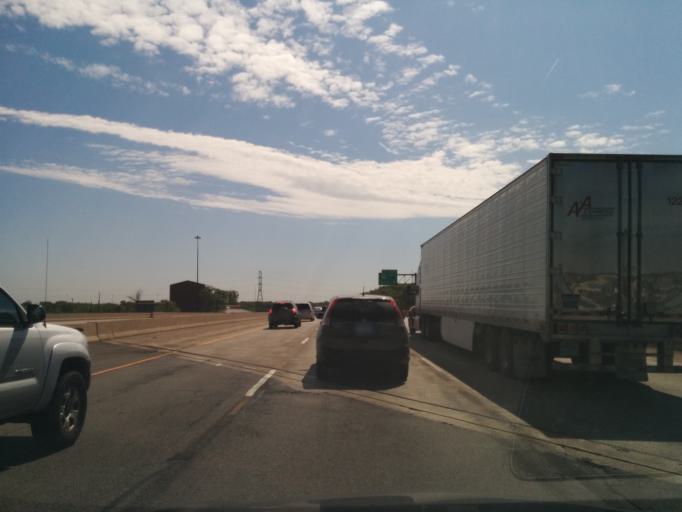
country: US
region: Indiana
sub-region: Porter County
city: Burns Harbor
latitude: 41.6071
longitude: -87.1088
